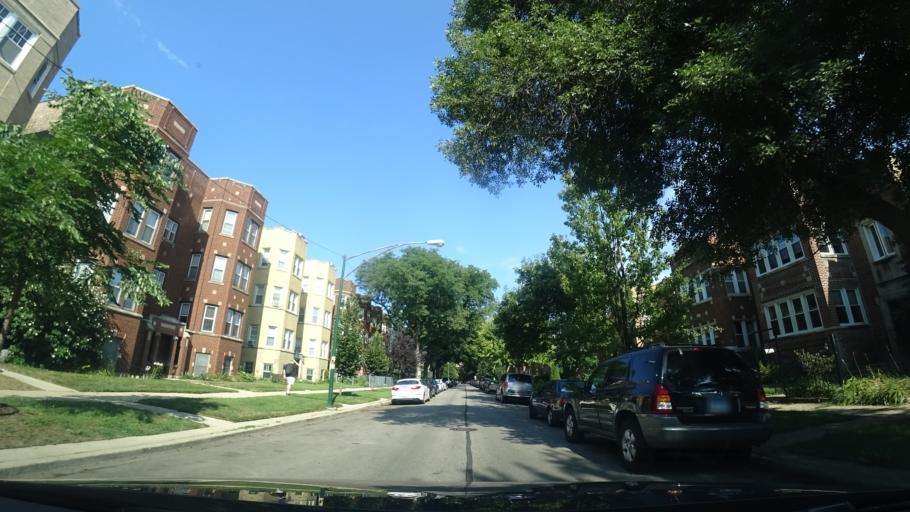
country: US
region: Illinois
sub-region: Cook County
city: Lincolnwood
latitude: 41.9731
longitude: -87.6961
